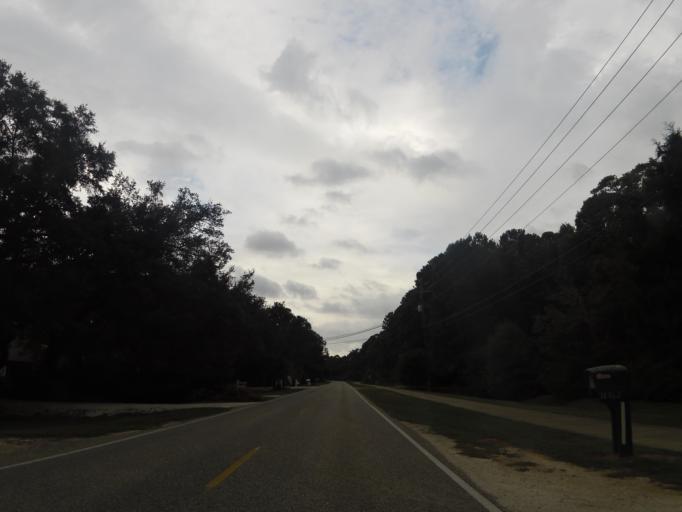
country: US
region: Alabama
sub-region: Baldwin County
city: Point Clear
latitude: 30.4423
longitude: -87.9120
